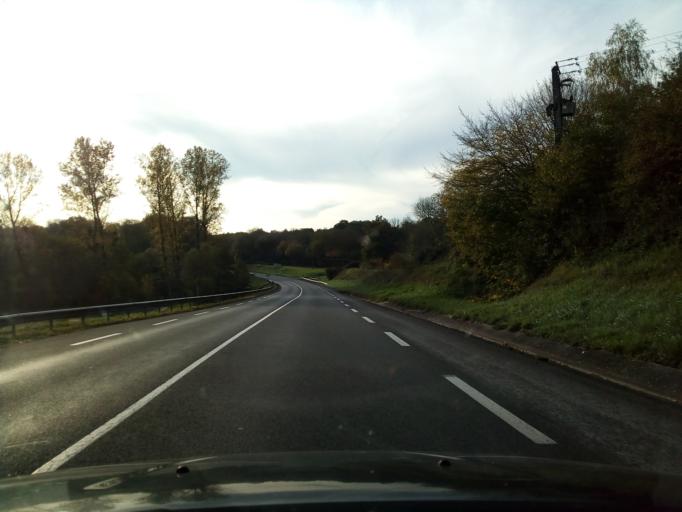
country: FR
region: Poitou-Charentes
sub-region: Departement de la Charente
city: Loubert
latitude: 45.9420
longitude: 0.5443
